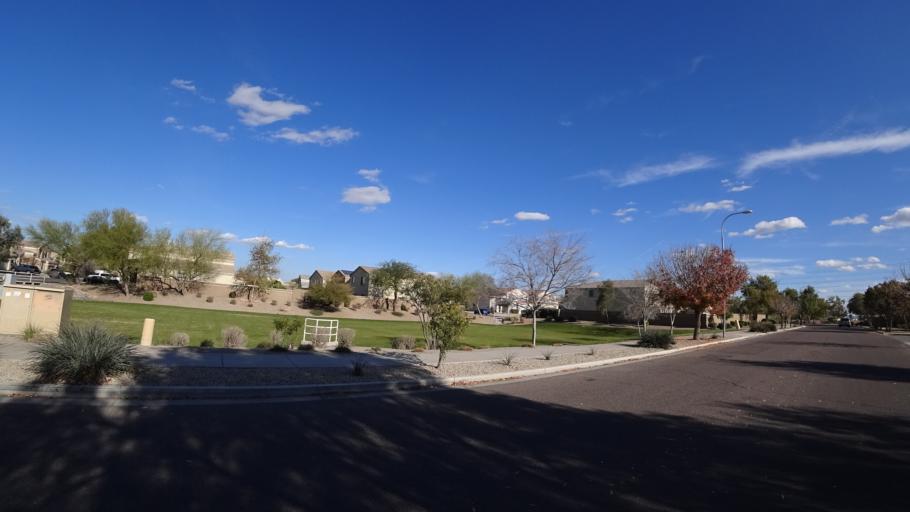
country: US
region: Arizona
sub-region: Maricopa County
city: Tolleson
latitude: 33.4173
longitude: -112.2417
